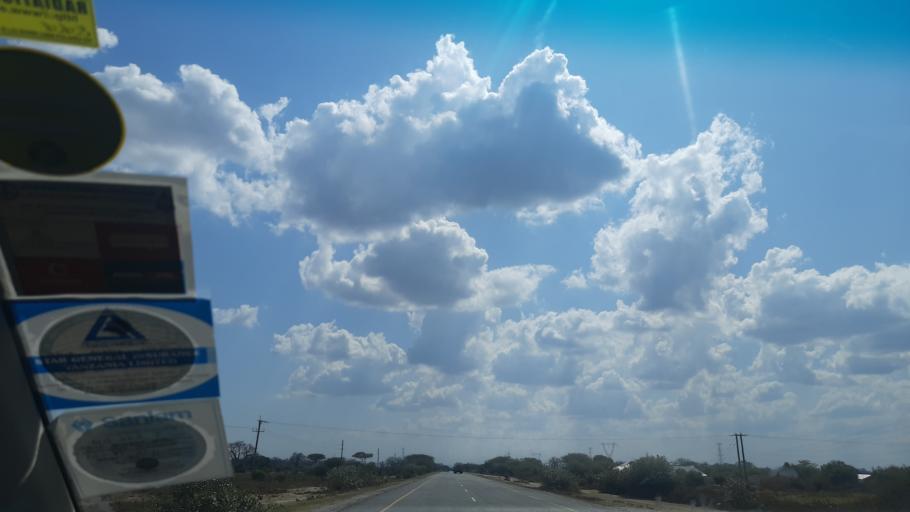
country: TZ
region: Singida
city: Kintinku
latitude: -5.9226
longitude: 35.2632
